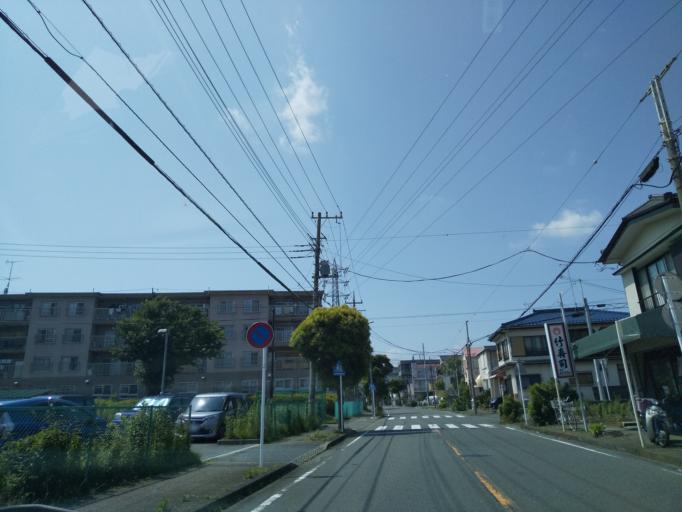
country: JP
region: Kanagawa
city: Zama
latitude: 35.5113
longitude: 139.4124
